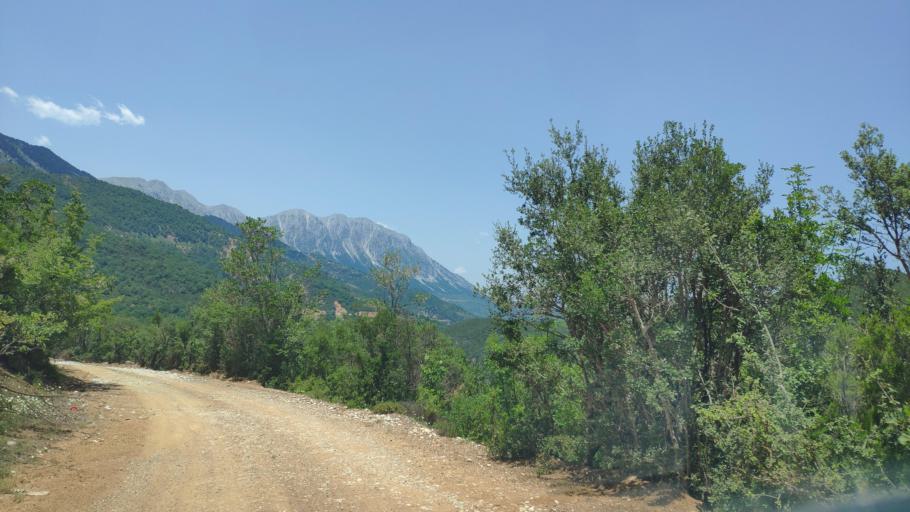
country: GR
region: Thessaly
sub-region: Nomos Kardhitsas
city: Anthiro
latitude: 39.1787
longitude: 21.3696
